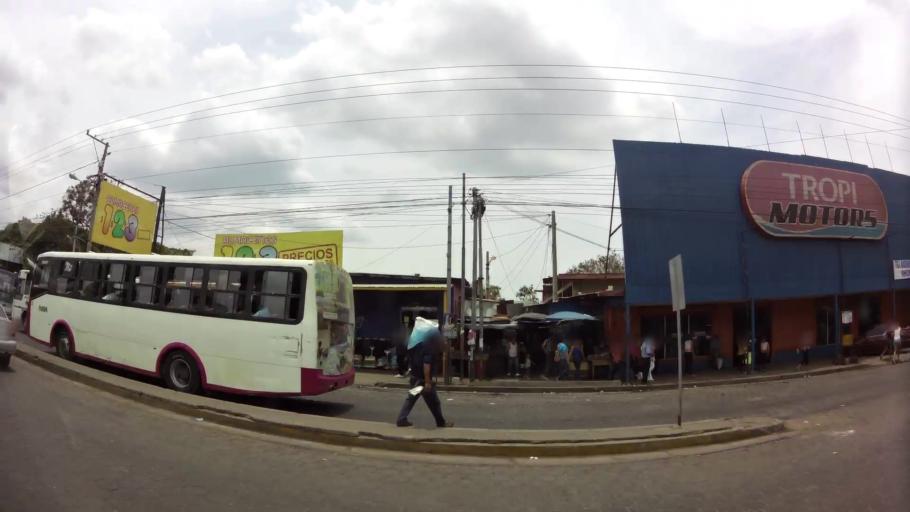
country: NI
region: Managua
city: Managua
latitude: 12.1240
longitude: -86.2420
